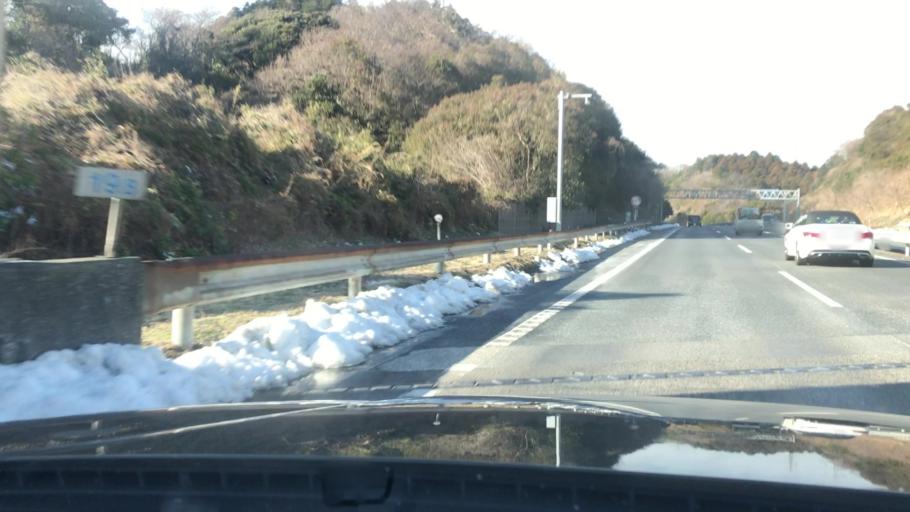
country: JP
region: Kanagawa
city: Zushi
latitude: 35.2965
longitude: 139.6175
